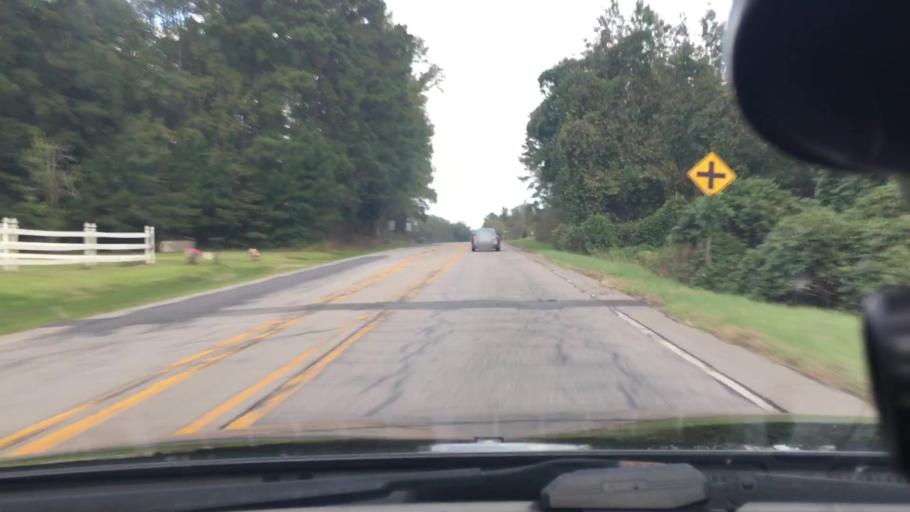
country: US
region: North Carolina
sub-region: Moore County
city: Carthage
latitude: 35.3557
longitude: -79.3429
